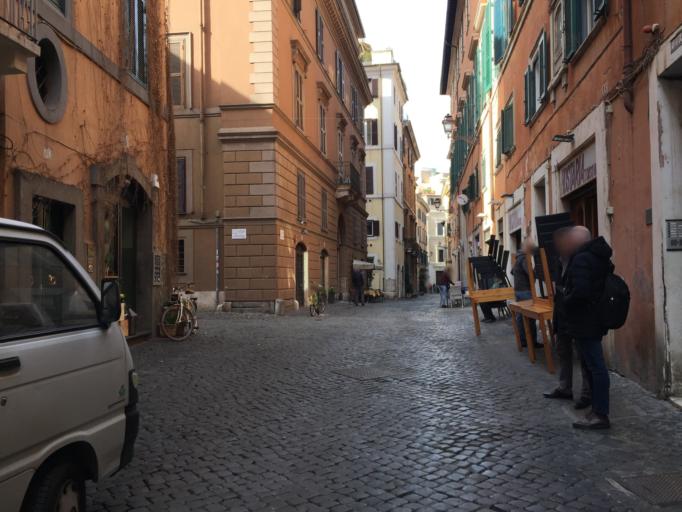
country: VA
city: Vatican City
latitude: 41.9018
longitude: 12.4739
